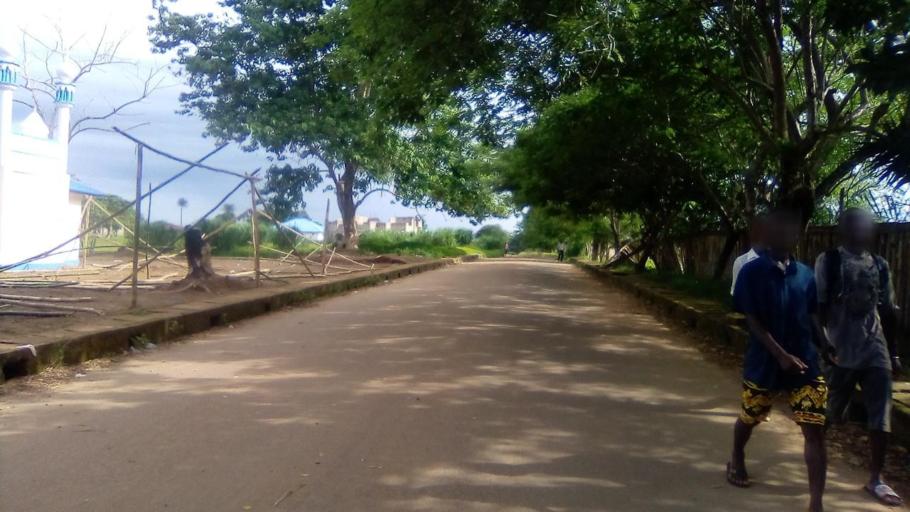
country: SL
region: Southern Province
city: Pujehun
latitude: 7.3685
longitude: -11.7265
